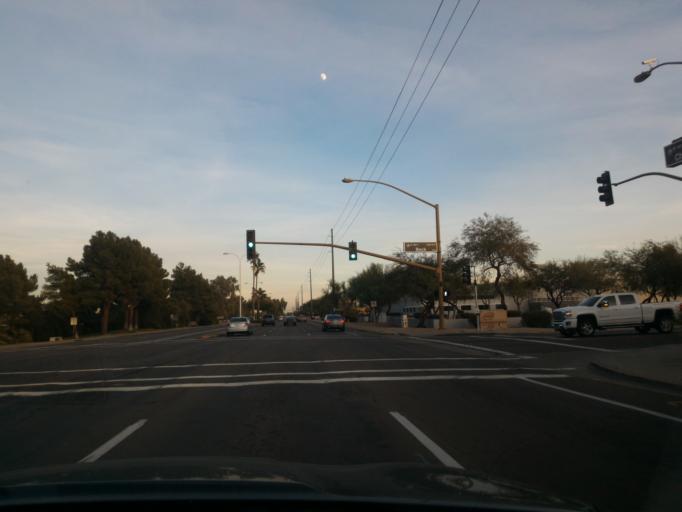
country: US
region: Arizona
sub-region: Maricopa County
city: Guadalupe
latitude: 33.3052
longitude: -111.9568
